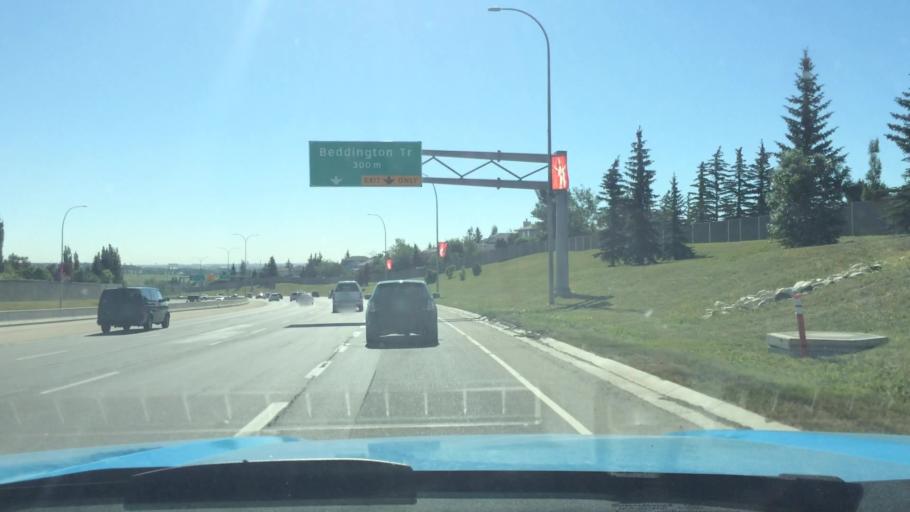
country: CA
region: Alberta
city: Calgary
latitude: 51.1425
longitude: -114.1043
